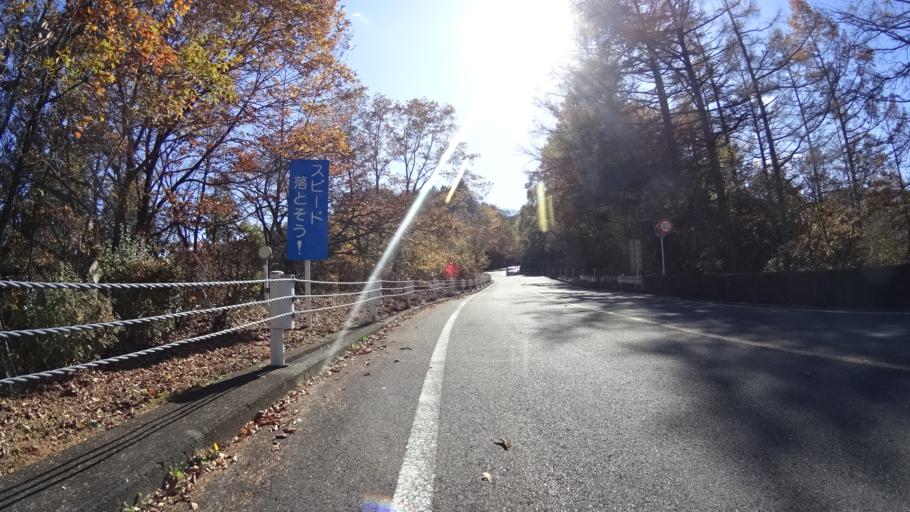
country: JP
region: Yamanashi
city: Uenohara
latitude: 35.7518
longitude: 139.0404
